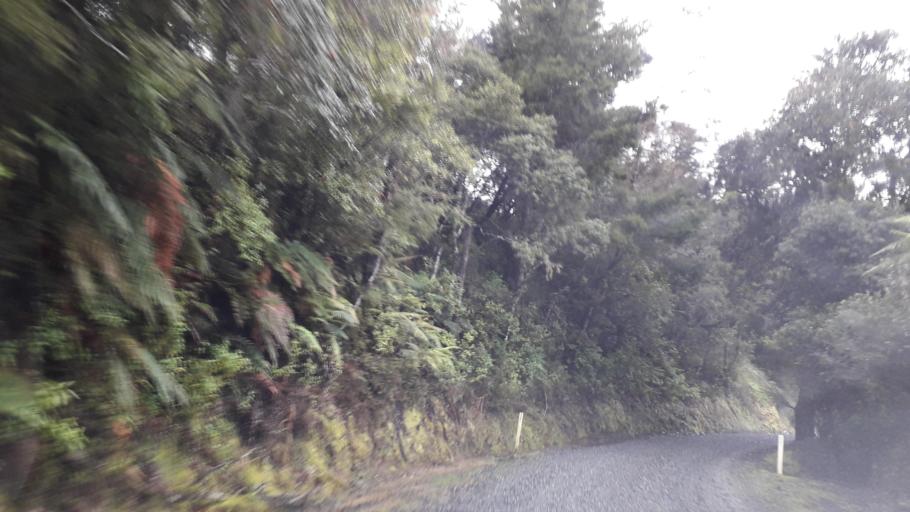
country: NZ
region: Northland
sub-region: Far North District
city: Waimate North
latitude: -35.1599
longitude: 173.7173
